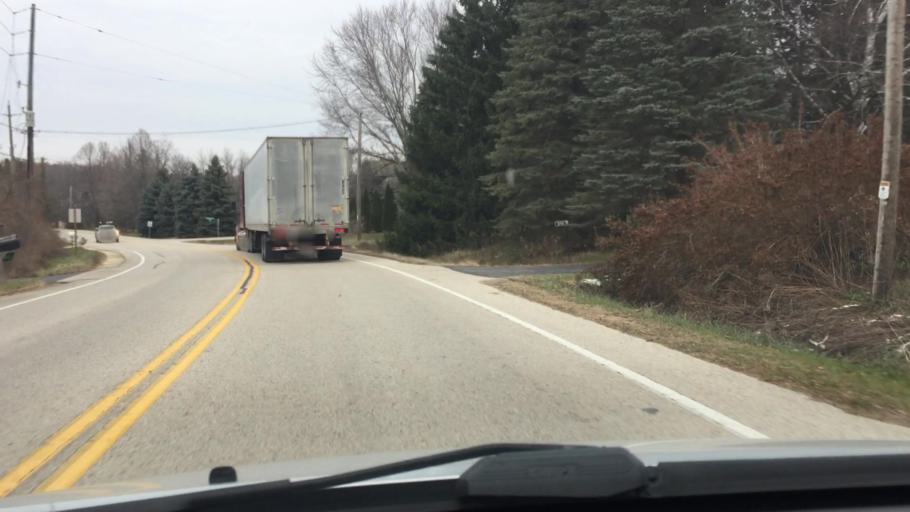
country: US
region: Wisconsin
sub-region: Ozaukee County
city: Grafton
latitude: 43.2965
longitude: -87.9596
